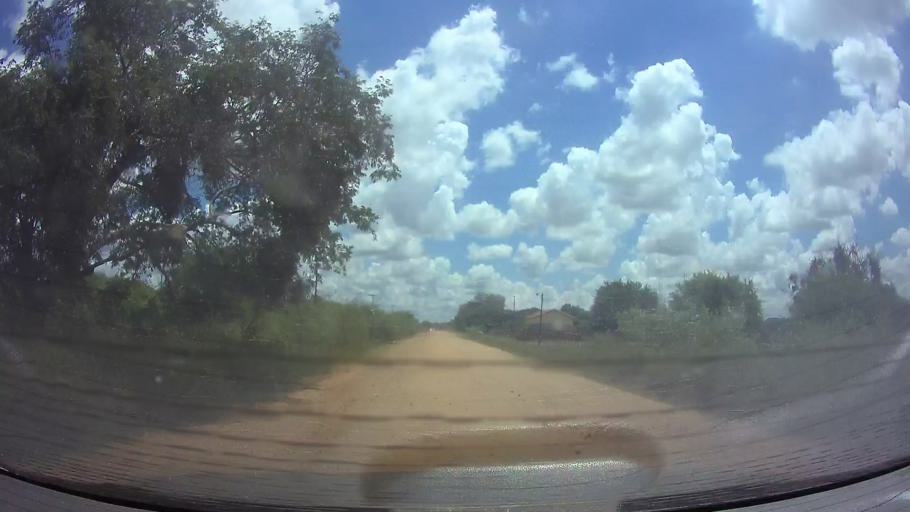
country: PY
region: Presidente Hayes
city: Nanawa
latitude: -25.2524
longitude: -57.6445
